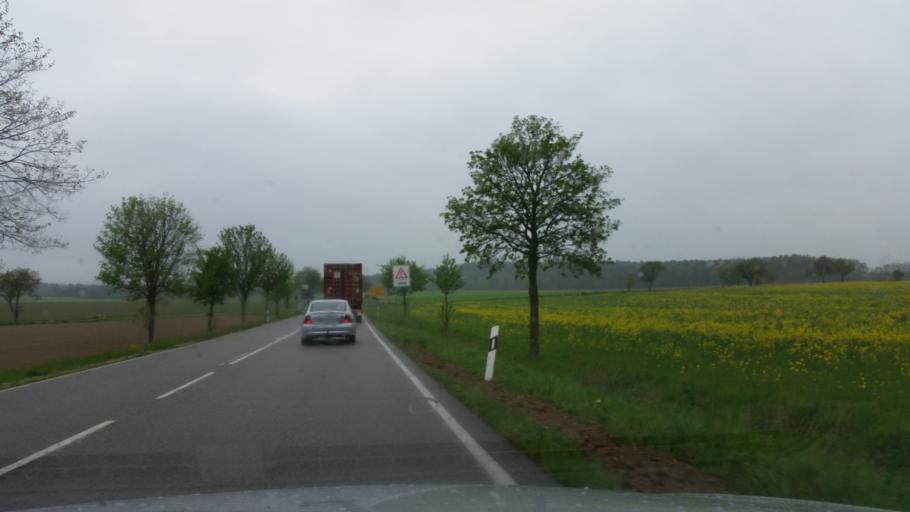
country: DE
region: Saxony-Anhalt
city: Kalbe
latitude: 52.6130
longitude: 11.3209
